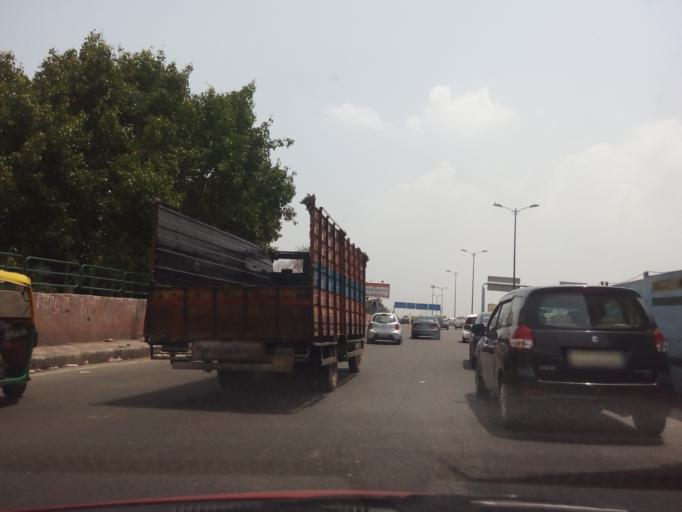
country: IN
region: NCT
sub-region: North West Delhi
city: Pitampura
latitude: 28.6331
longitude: 77.1318
